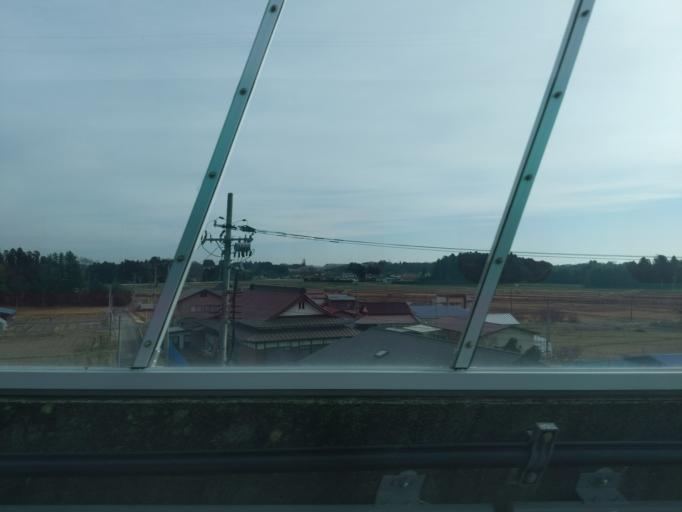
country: JP
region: Iwate
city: Ichinoseki
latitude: 38.7460
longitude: 141.0701
